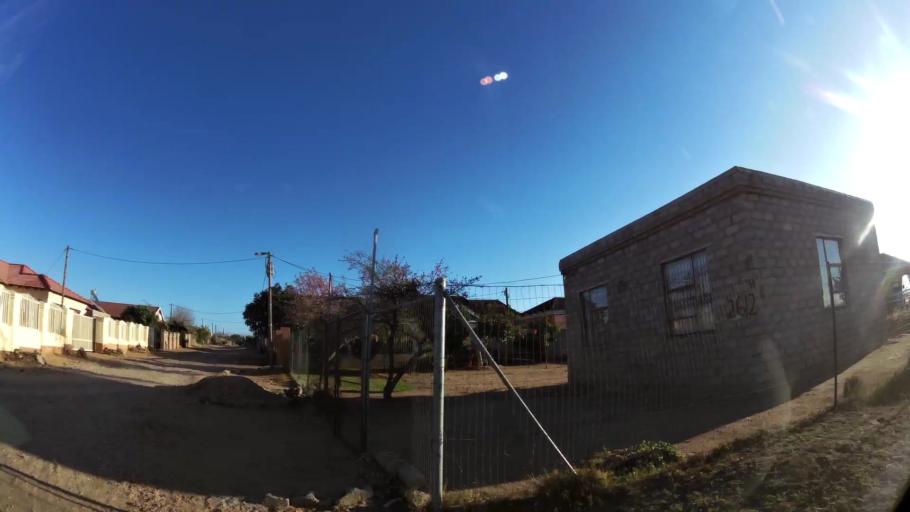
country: ZA
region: Limpopo
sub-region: Capricorn District Municipality
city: Polokwane
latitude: -23.8413
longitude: 29.3639
